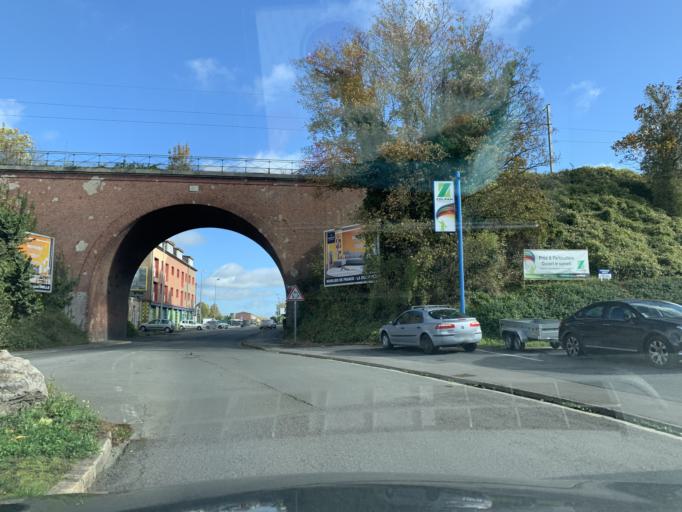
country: FR
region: Nord-Pas-de-Calais
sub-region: Departement du Nord
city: Neuville-Saint-Remy
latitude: 50.1821
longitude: 3.2333
